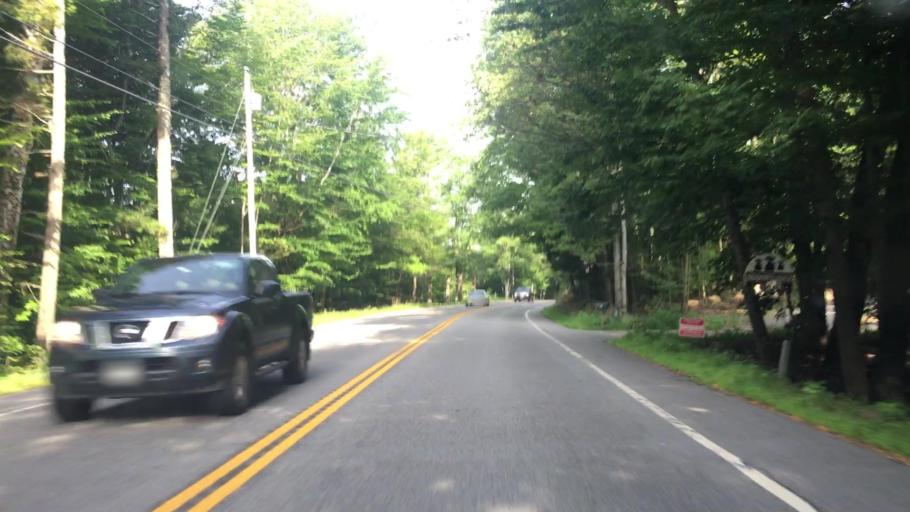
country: US
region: Maine
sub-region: York County
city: Limington
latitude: 43.7770
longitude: -70.7424
